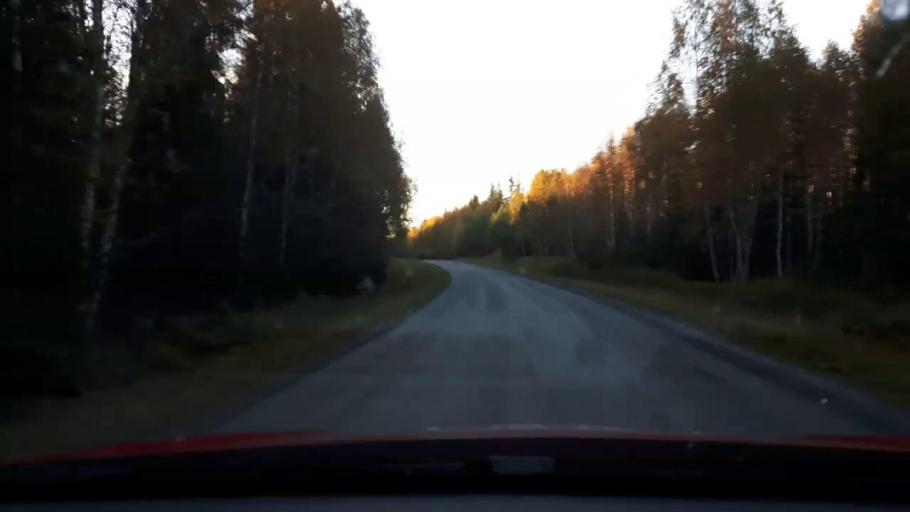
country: SE
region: Jaemtland
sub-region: Krokoms Kommun
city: Krokom
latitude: 63.4599
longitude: 14.3974
